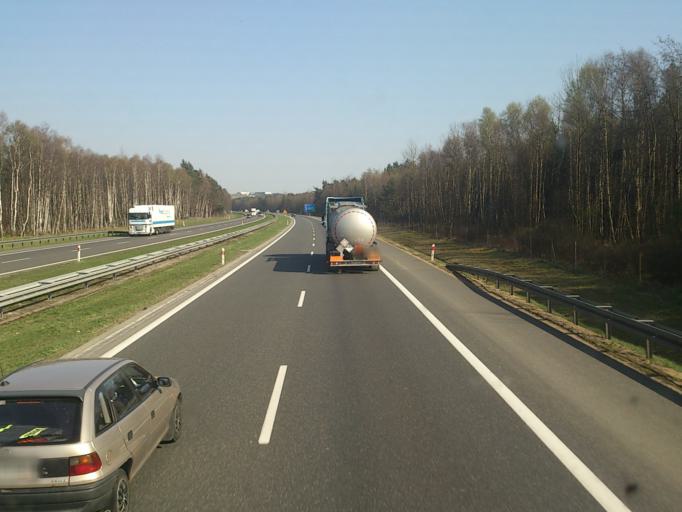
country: PL
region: Lesser Poland Voivodeship
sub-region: Powiat chrzanowski
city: Regulice
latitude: 50.1080
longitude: 19.5162
